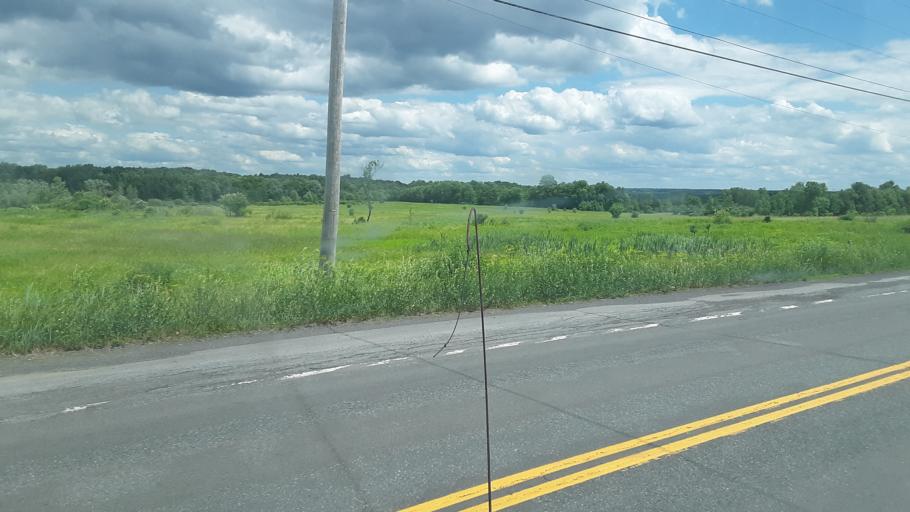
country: US
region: New York
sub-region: Oneida County
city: Boonville
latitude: 43.3918
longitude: -75.4887
